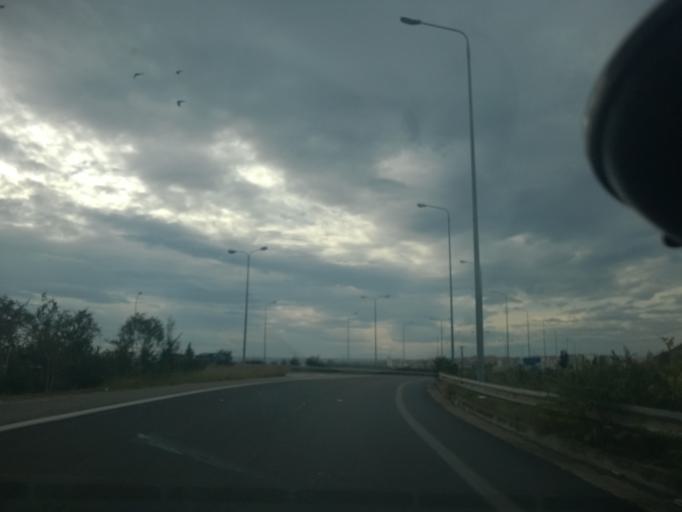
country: GR
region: Central Macedonia
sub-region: Nomos Thessalonikis
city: Pylaia
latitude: 40.5806
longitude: 22.9755
